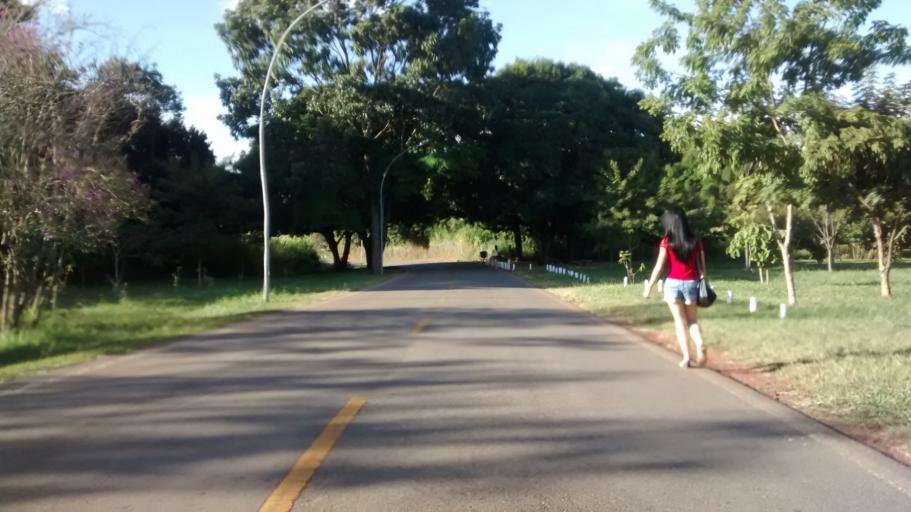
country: BR
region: Federal District
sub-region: Brasilia
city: Brasilia
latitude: -15.8316
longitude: -48.0228
